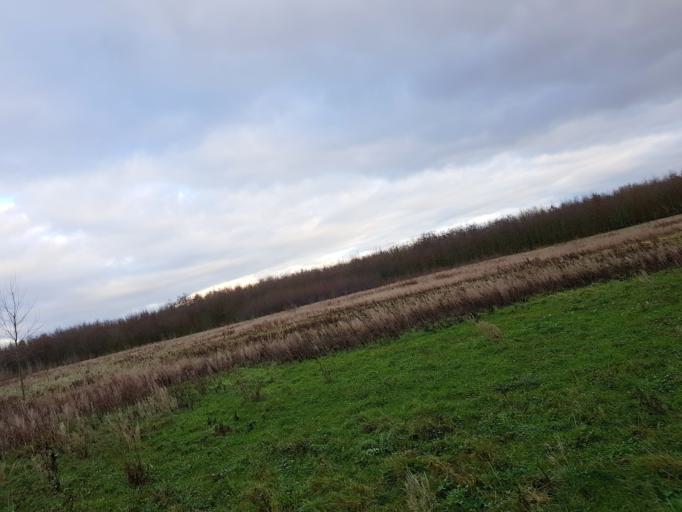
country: NL
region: South Holland
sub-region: Gemeente Rijnwoude
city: Benthuizen
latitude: 52.0711
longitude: 4.5917
